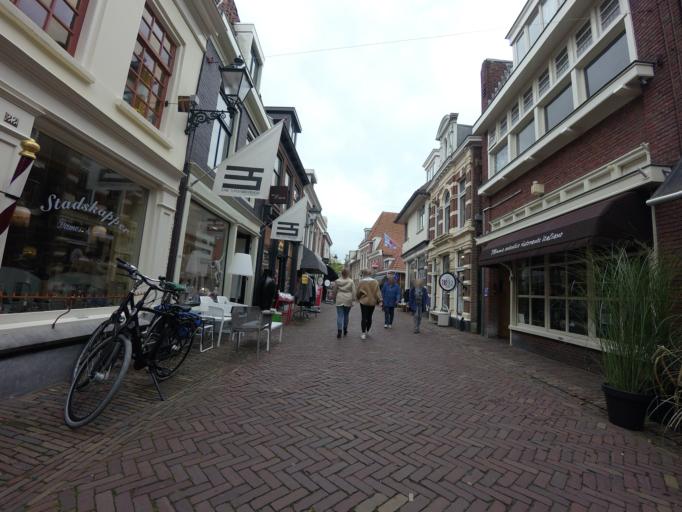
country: NL
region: Friesland
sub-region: Gemeente Leeuwarden
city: Bilgaard
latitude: 53.2023
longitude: 5.7916
